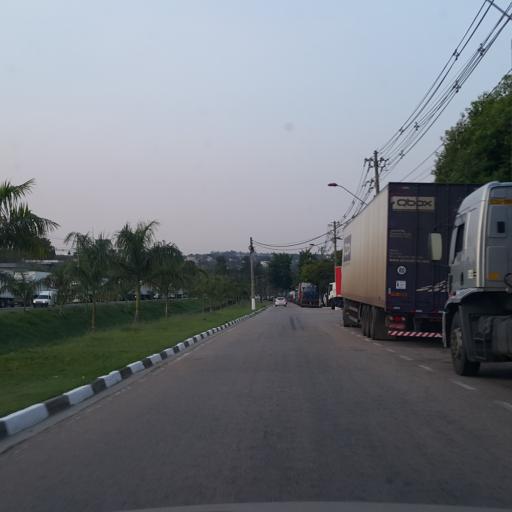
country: BR
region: Sao Paulo
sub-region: Vinhedo
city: Vinhedo
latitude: -23.0669
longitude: -47.0006
